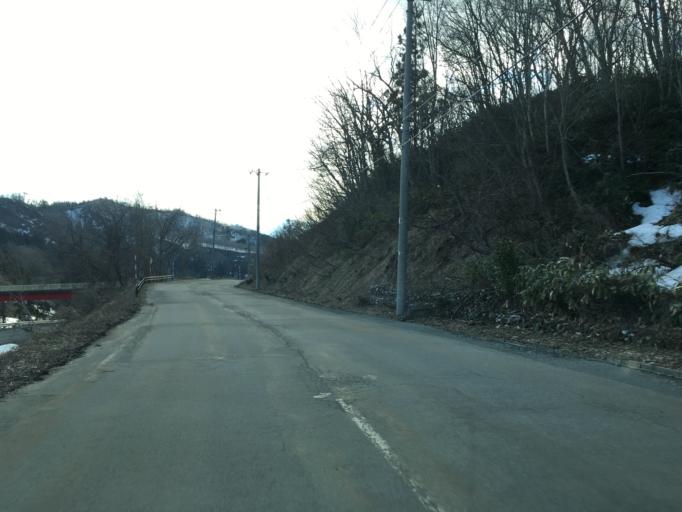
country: JP
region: Yamagata
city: Yonezawa
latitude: 37.9290
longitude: 139.9138
